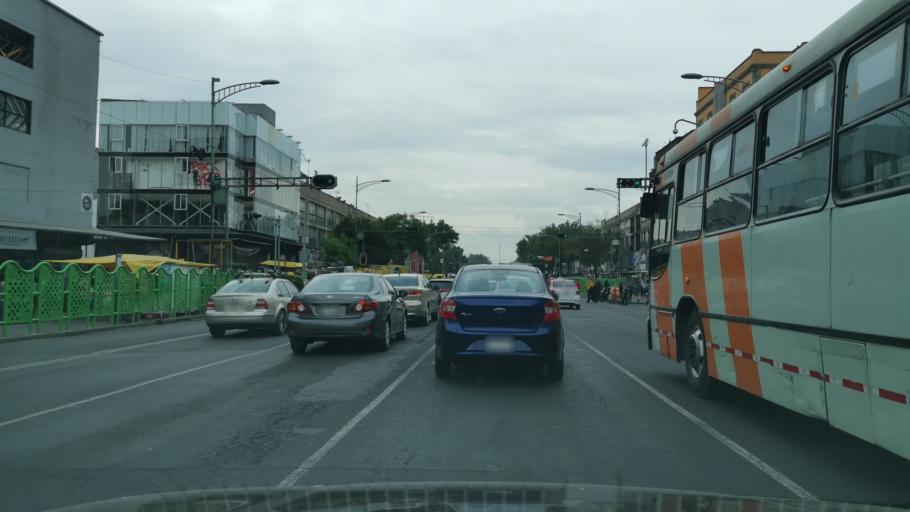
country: MX
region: Mexico City
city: Mexico City
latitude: 19.4368
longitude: -99.1239
